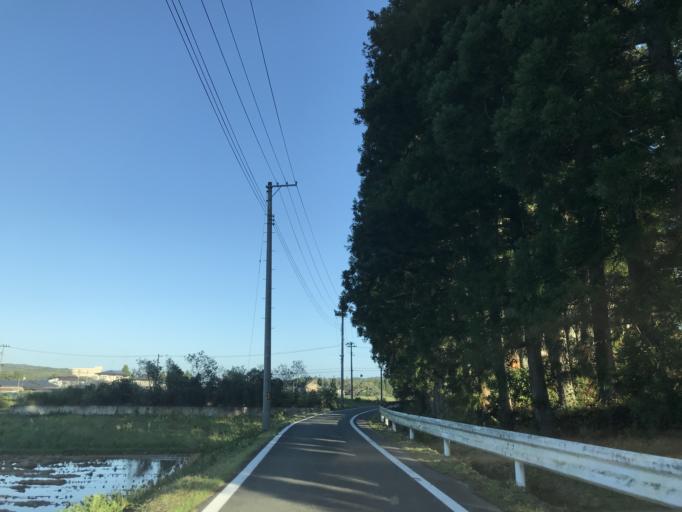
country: JP
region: Iwate
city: Ichinoseki
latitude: 38.9419
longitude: 141.0467
